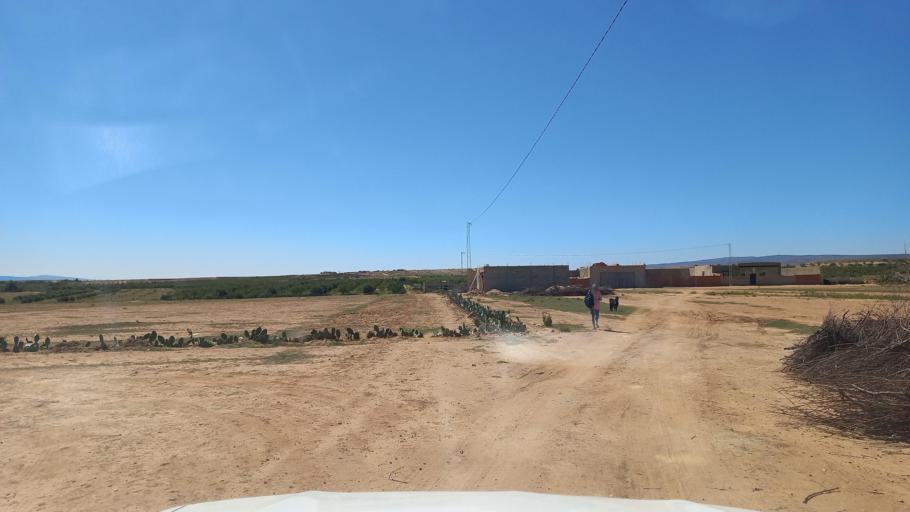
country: TN
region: Al Qasrayn
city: Sbiba
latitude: 35.3591
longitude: 9.0880
